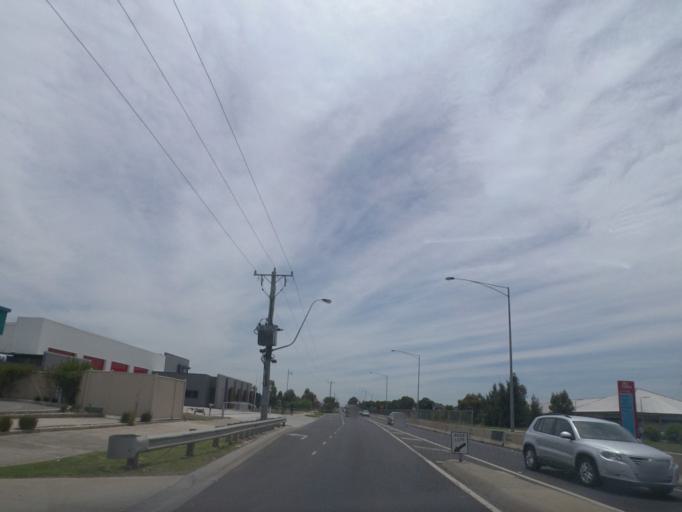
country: AU
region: Victoria
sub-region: Wyndham
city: Tarneit
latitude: -37.8476
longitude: 144.6883
